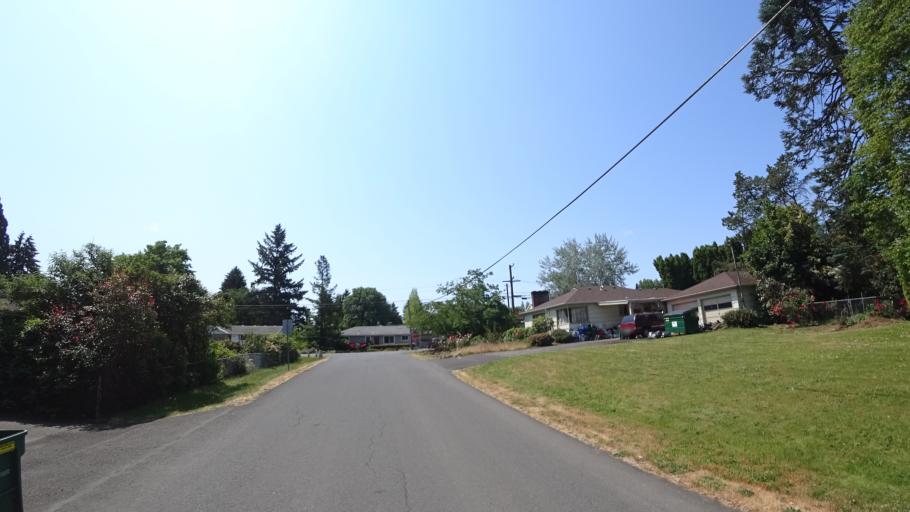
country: US
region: Oregon
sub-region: Clackamas County
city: Oatfield
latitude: 45.4450
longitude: -122.5954
